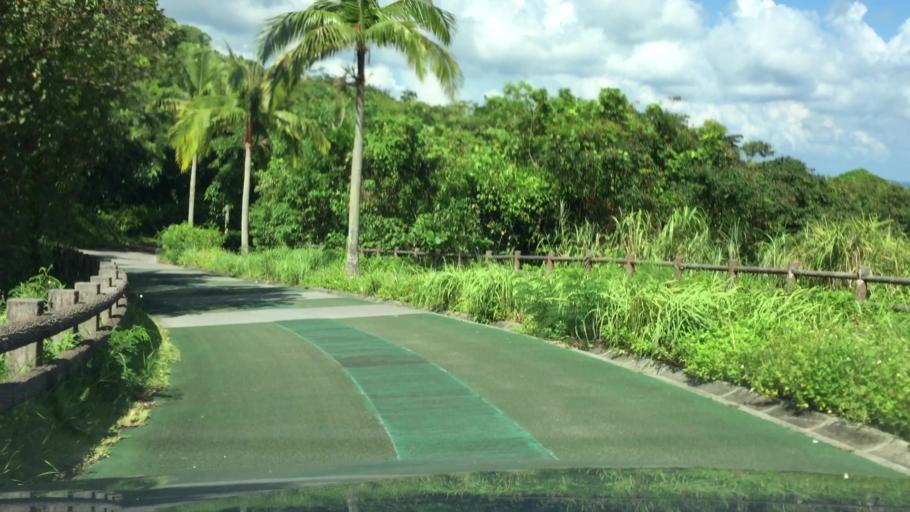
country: JP
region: Okinawa
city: Ishigaki
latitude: 24.3866
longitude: 124.1653
